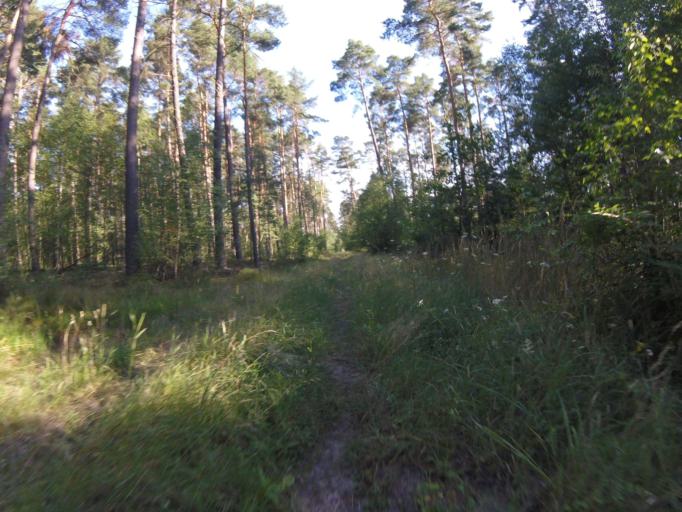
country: DE
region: Berlin
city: Schmockwitz
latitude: 52.3397
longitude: 13.7197
